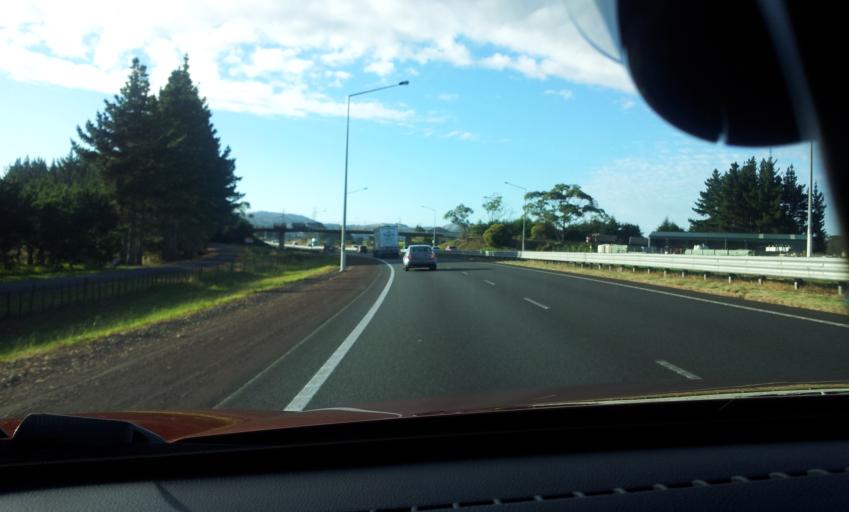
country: NZ
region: Auckland
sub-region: Auckland
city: Papakura
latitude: -37.1159
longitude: 174.9495
